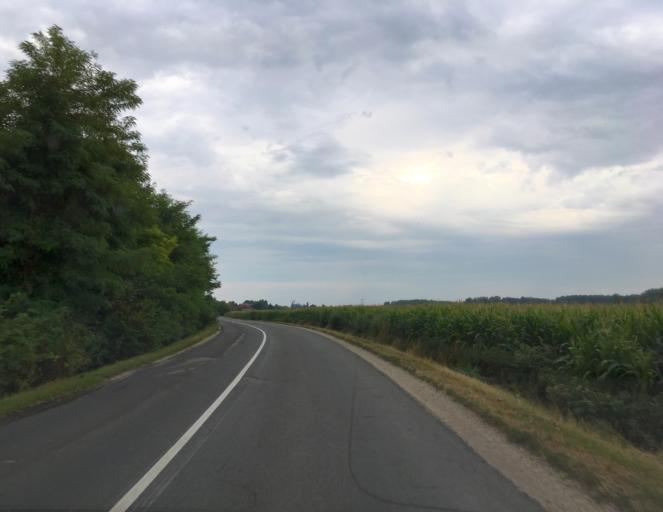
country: SK
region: Trnavsky
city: Gabcikovo
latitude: 47.8840
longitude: 17.6580
